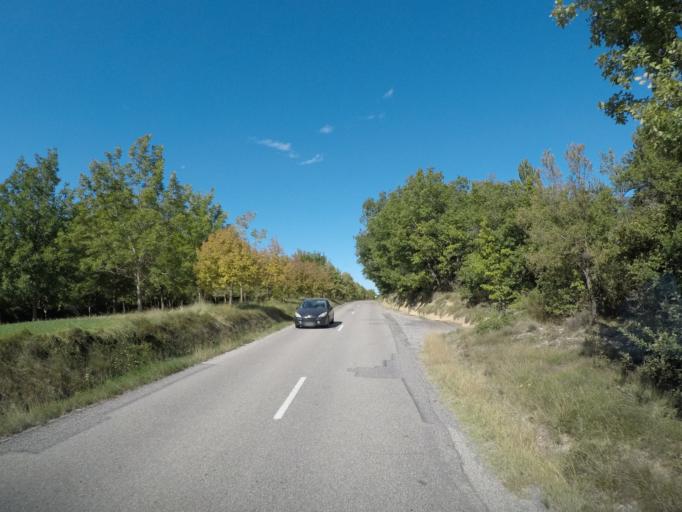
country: FR
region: Provence-Alpes-Cote d'Azur
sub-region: Departement des Alpes-de-Haute-Provence
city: Mallemoisson
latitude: 44.0130
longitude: 6.1844
